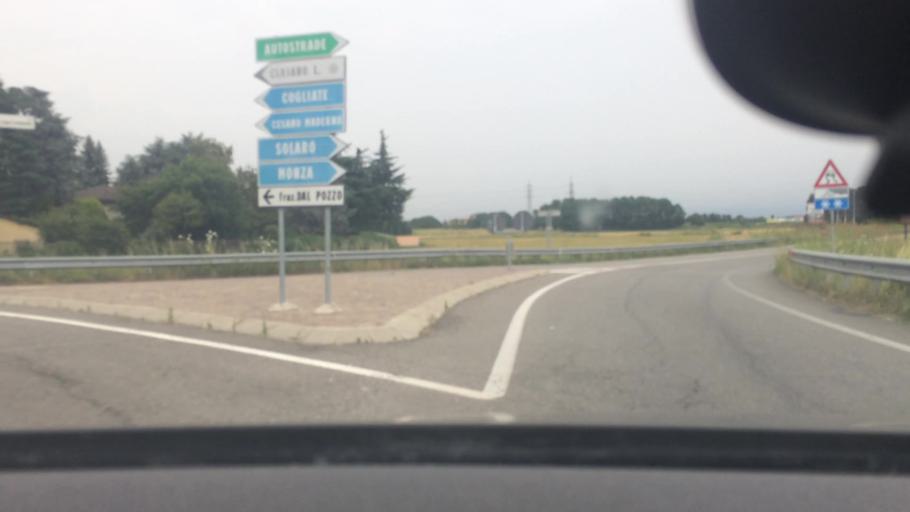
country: IT
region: Lombardy
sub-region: Provincia di Monza e Brianza
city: Ceriano Laghetto
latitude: 45.6290
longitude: 9.0602
